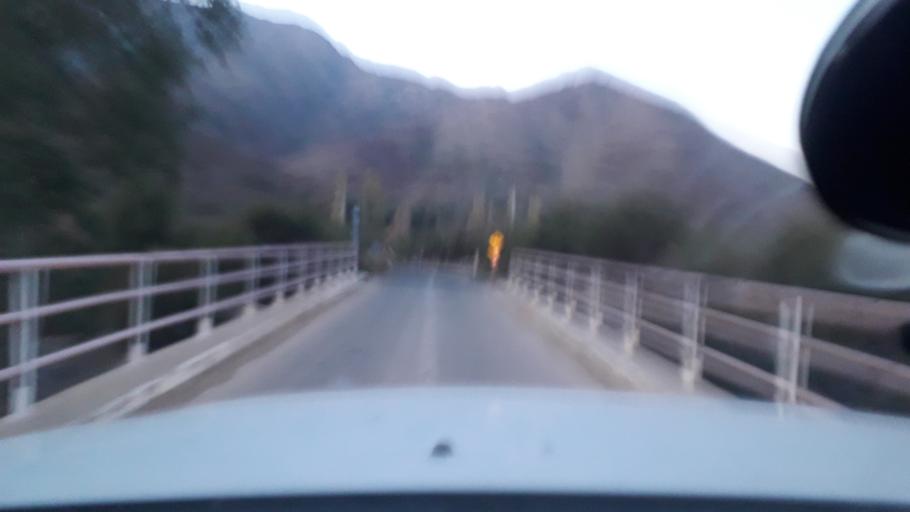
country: CL
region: Valparaiso
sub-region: Provincia de Marga Marga
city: Limache
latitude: -33.1737
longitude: -71.1286
